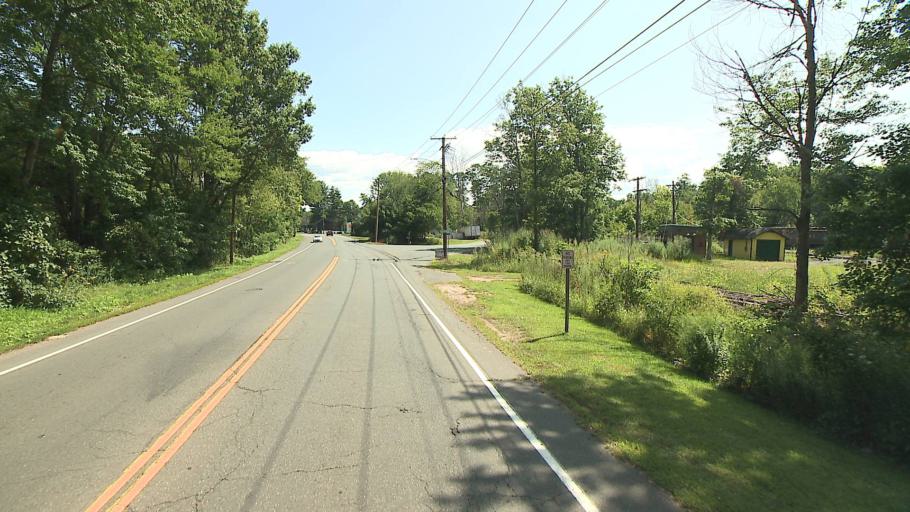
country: US
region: Connecticut
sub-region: Hartford County
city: Windsor Locks
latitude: 41.9321
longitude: -72.5942
